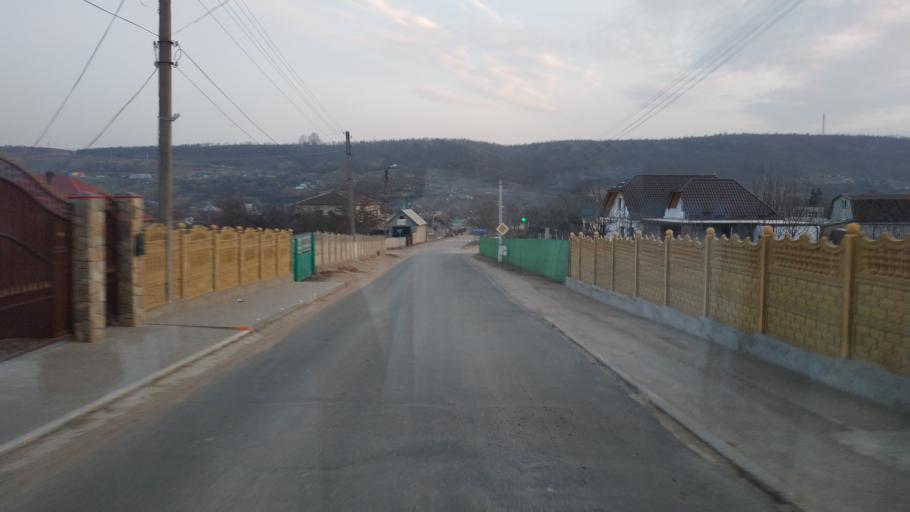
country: MD
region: Hincesti
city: Dancu
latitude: 46.6675
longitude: 28.3283
